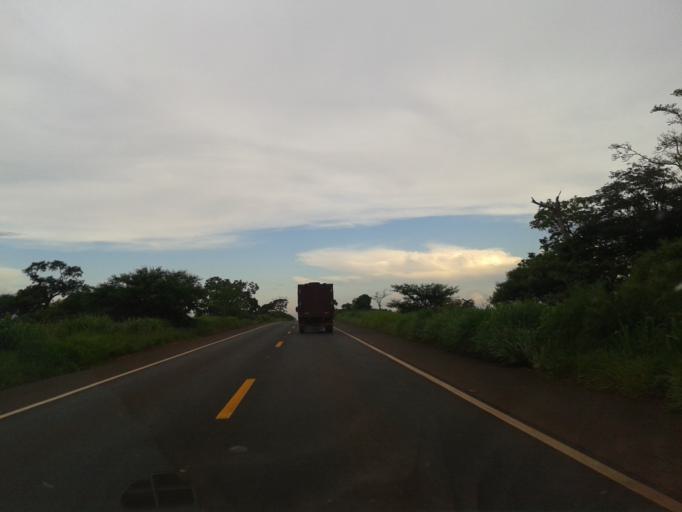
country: BR
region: Minas Gerais
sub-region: Santa Vitoria
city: Santa Vitoria
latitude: -18.8854
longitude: -50.1482
